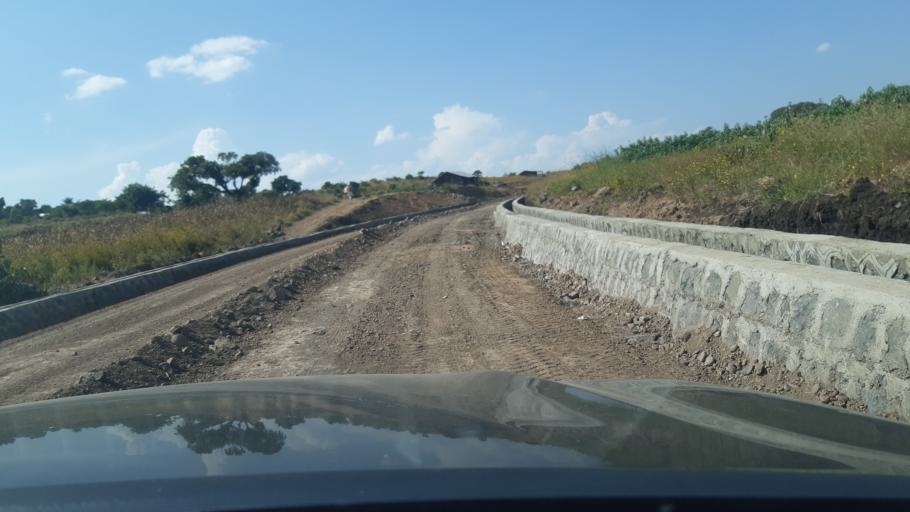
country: ET
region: Amhara
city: Dabat
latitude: 13.1597
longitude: 37.6080
